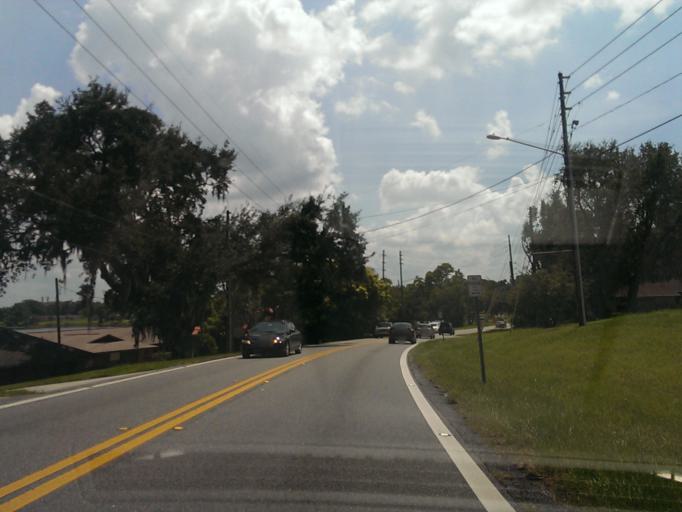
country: US
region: Florida
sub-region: Orange County
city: Doctor Phillips
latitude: 28.4880
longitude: -81.4752
